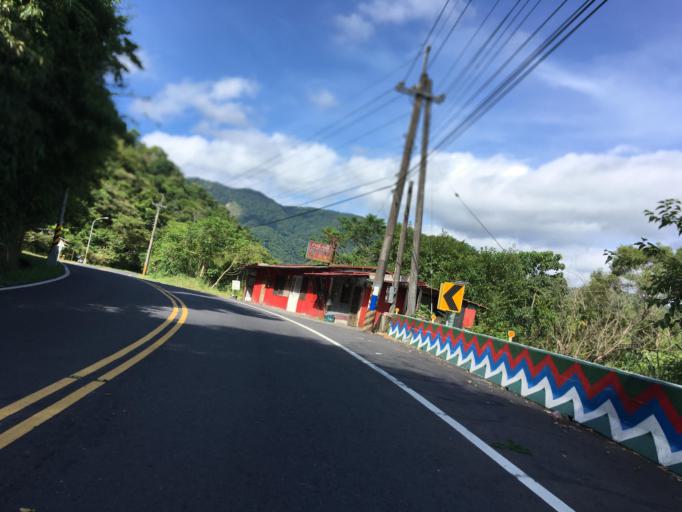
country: TW
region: Taiwan
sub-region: Yilan
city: Yilan
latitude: 24.6158
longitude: 121.6944
